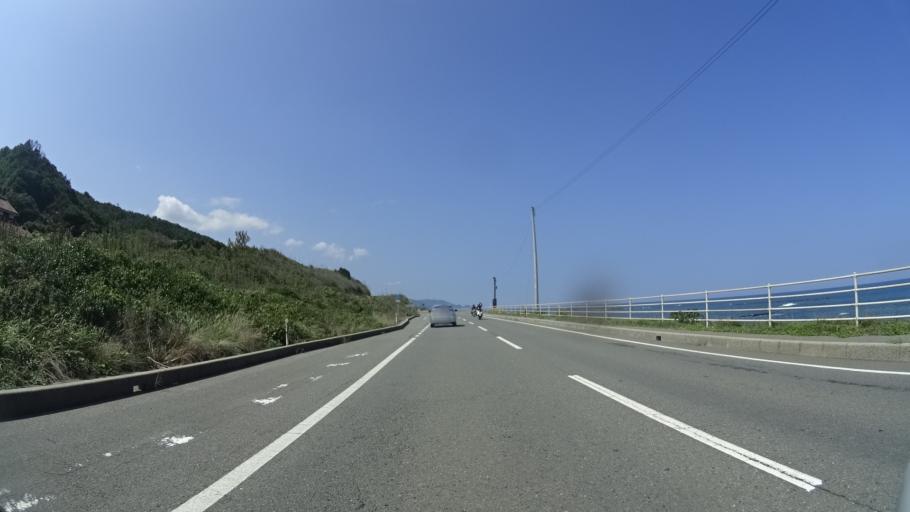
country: JP
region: Shimane
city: Masuda
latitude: 34.6860
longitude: 131.7889
